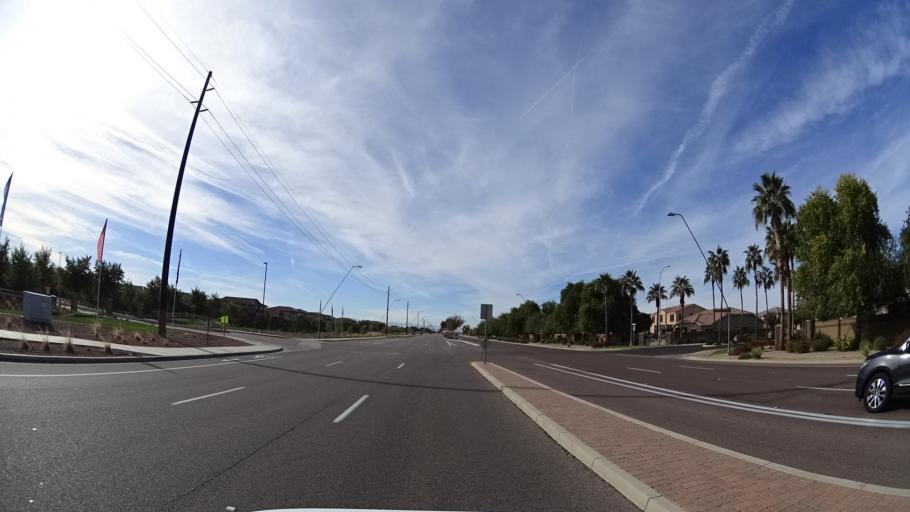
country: US
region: Arizona
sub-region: Maricopa County
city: Chandler
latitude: 33.2629
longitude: -111.7830
